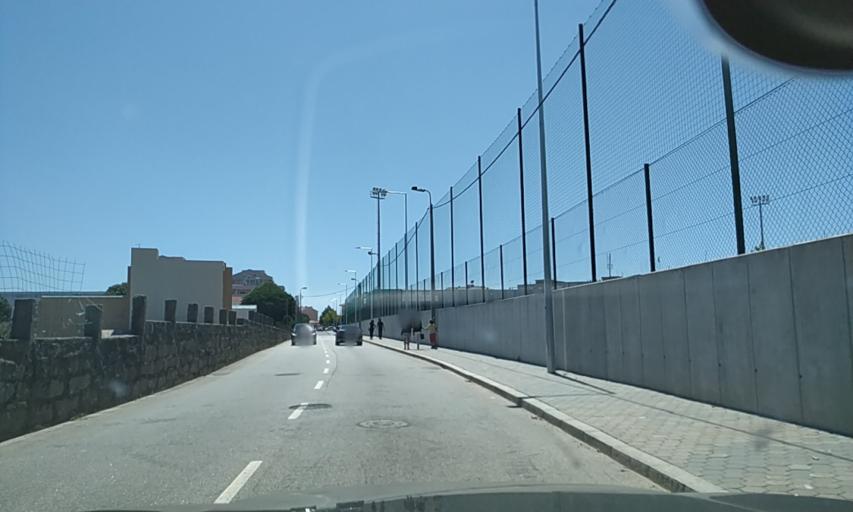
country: PT
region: Porto
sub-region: Vila Nova de Gaia
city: Canidelo
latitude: 41.1332
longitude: -8.6452
